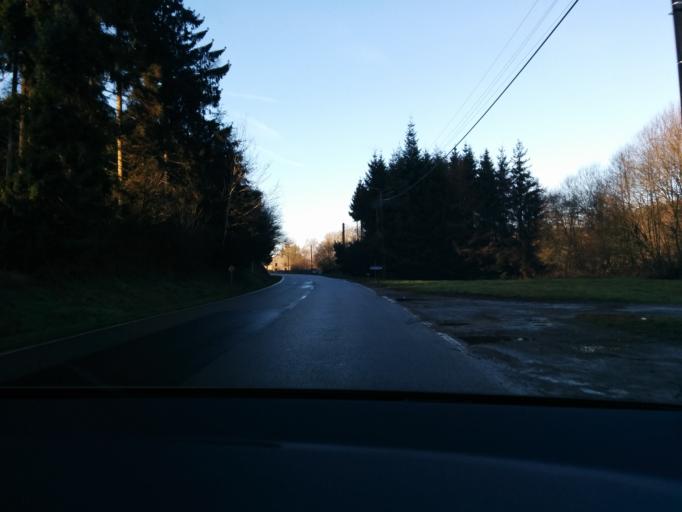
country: BE
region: Wallonia
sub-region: Province du Luxembourg
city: Vielsalm
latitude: 50.2682
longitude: 5.8844
